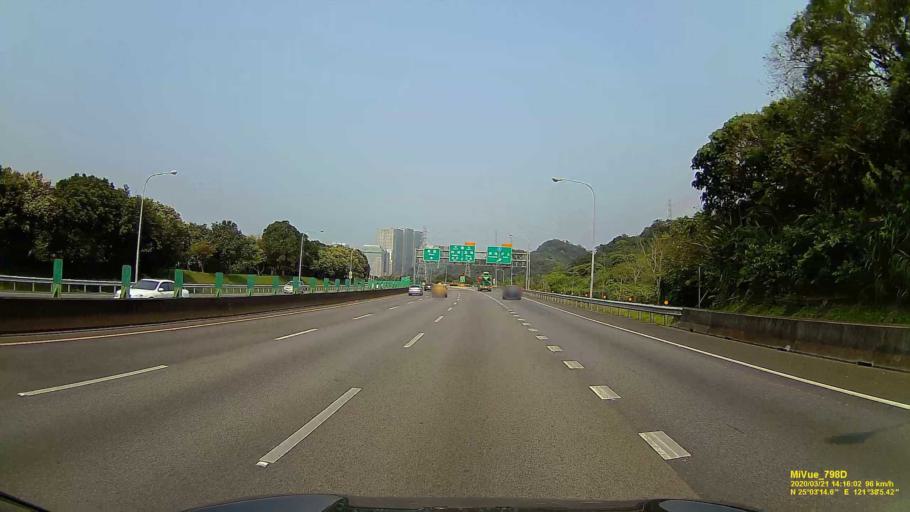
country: TW
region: Taipei
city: Taipei
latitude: 25.0545
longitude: 121.6347
